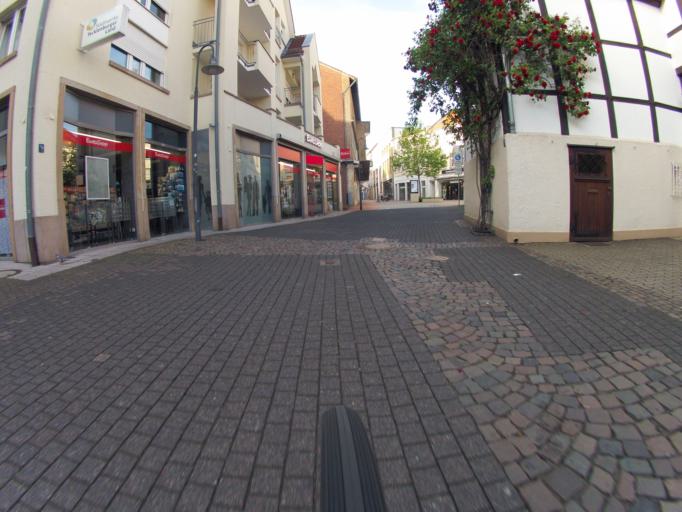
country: DE
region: North Rhine-Westphalia
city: Ibbenburen
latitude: 52.2764
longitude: 7.7151
